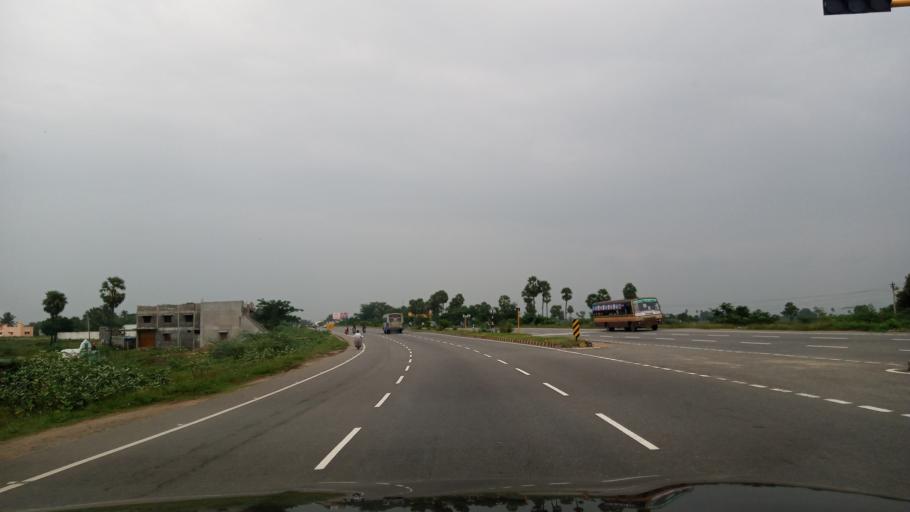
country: IN
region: Tamil Nadu
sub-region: Vellore
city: Pallikondai
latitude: 12.9124
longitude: 79.0159
